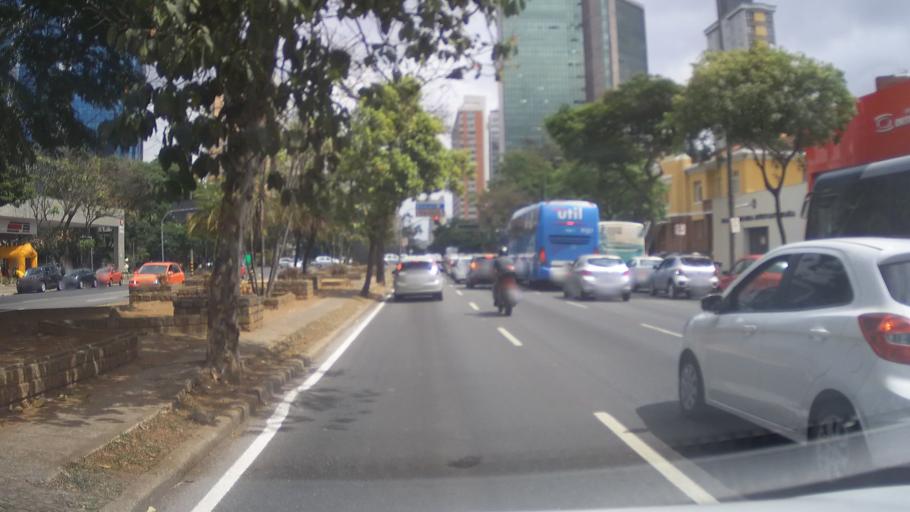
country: BR
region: Minas Gerais
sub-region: Belo Horizonte
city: Belo Horizonte
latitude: -19.9309
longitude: -43.9312
